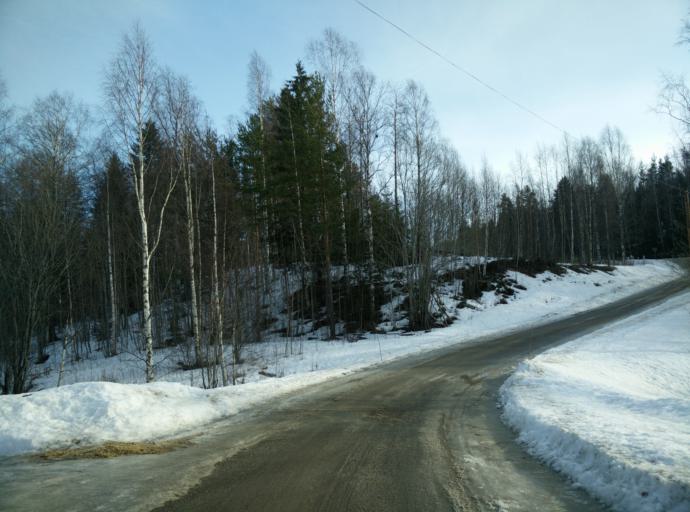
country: SE
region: Vaesternorrland
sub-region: Sundsvalls Kommun
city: Njurundabommen
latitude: 62.2023
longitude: 17.2707
